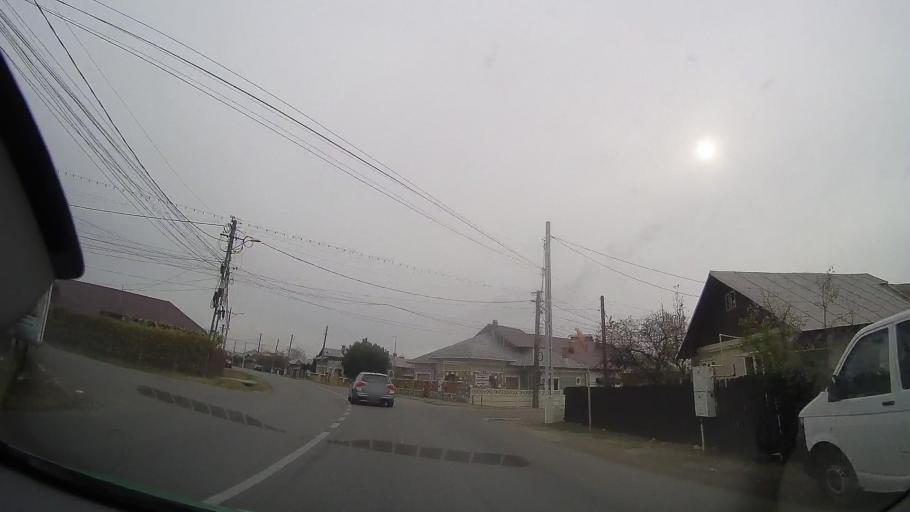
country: RO
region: Prahova
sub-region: Oras Baicoi
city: Tintea
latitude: 45.0316
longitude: 25.9047
